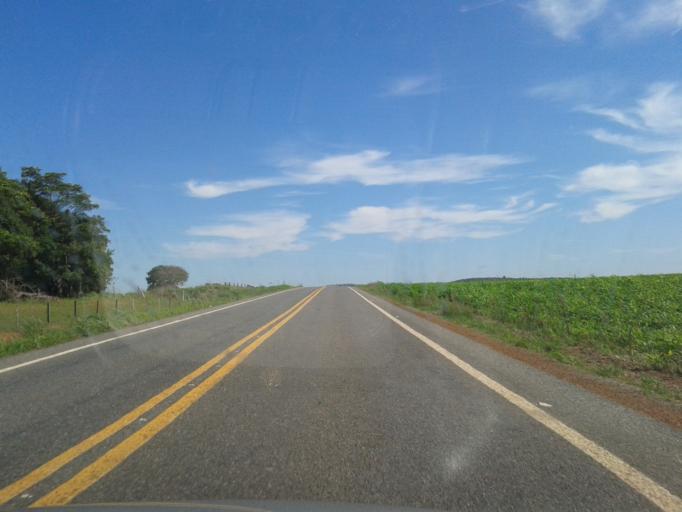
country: BR
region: Goias
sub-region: Piracanjuba
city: Piracanjuba
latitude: -17.3223
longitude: -48.8007
